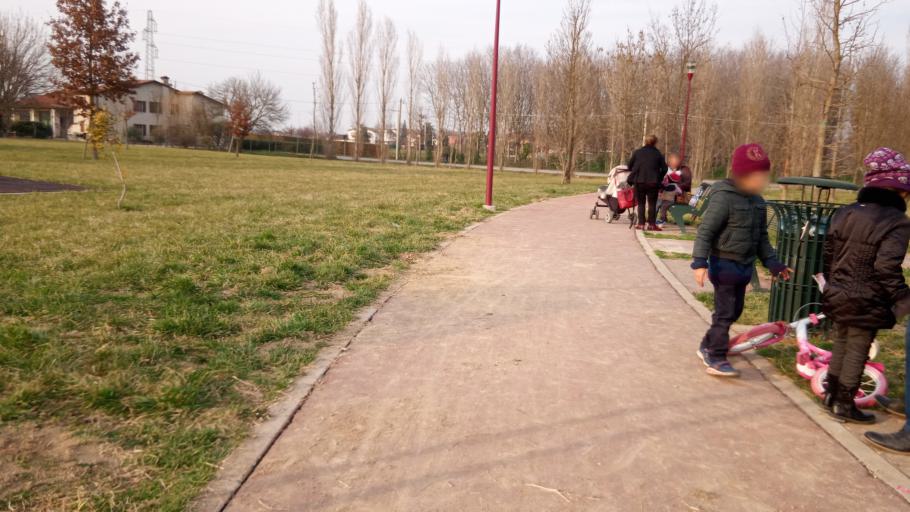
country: IT
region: Veneto
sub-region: Provincia di Padova
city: Rubano
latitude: 45.4319
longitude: 11.7818
